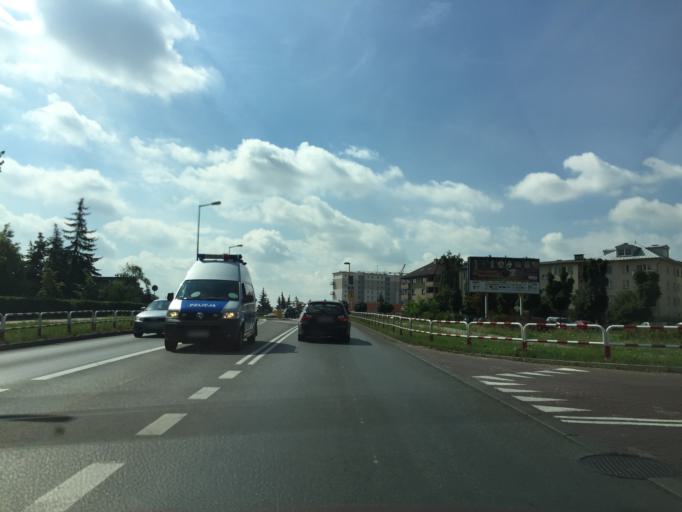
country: PL
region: Greater Poland Voivodeship
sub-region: Kalisz
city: Kalisz
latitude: 51.7520
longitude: 18.0611
